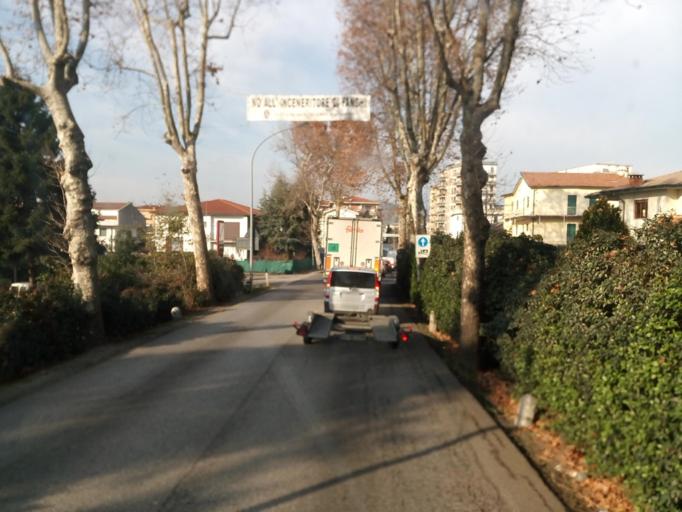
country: IT
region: Veneto
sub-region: Provincia di Vicenza
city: Brendola
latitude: 45.4914
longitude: 11.4351
